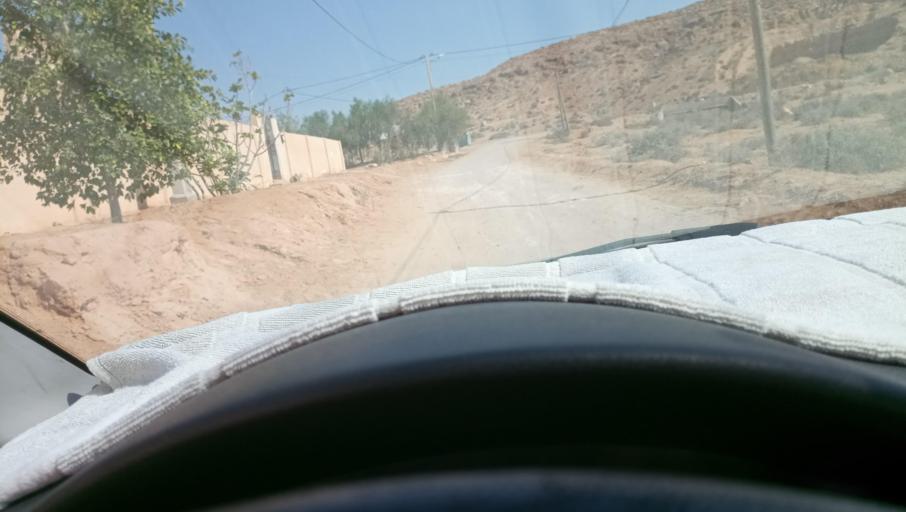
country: TN
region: Tataouine
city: Tataouine
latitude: 32.9833
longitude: 10.3806
